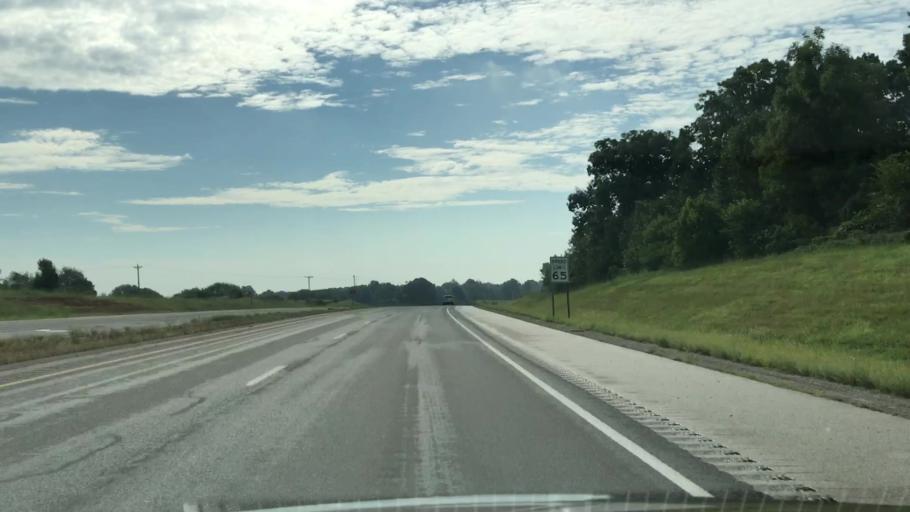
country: US
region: Kentucky
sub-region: Warren County
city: Plano
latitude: 36.8596
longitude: -86.3437
